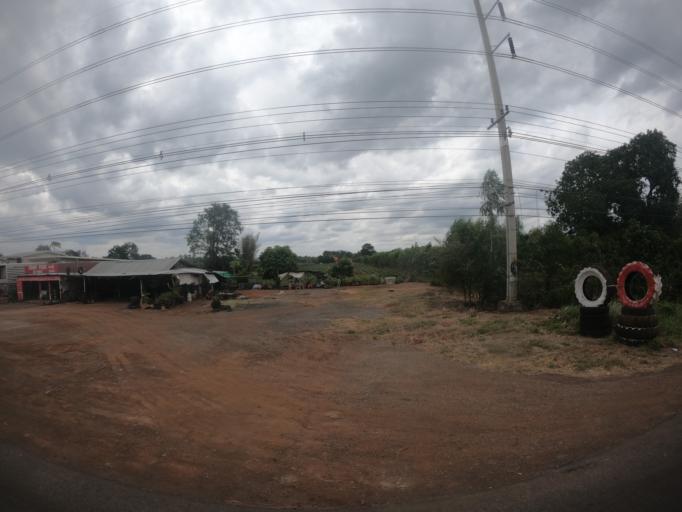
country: TH
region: Nakhon Ratchasima
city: Nong Bun Nak
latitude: 14.7555
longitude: 102.3221
